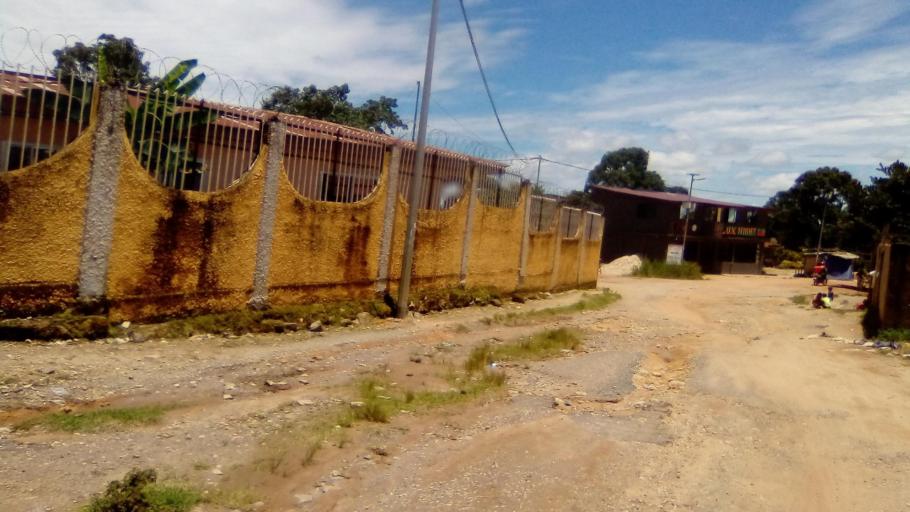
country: SL
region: Eastern Province
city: Koidu
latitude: 8.6309
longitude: -10.9918
